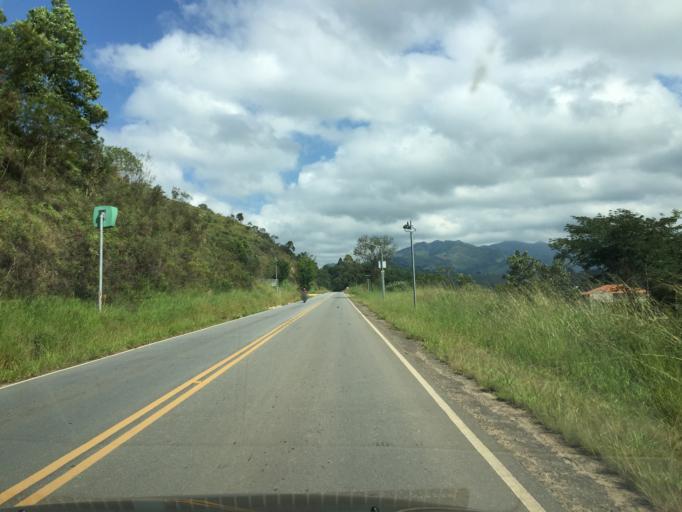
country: BR
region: Minas Gerais
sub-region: Passa Quatro
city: Passa Quatro
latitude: -22.3756
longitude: -44.9621
